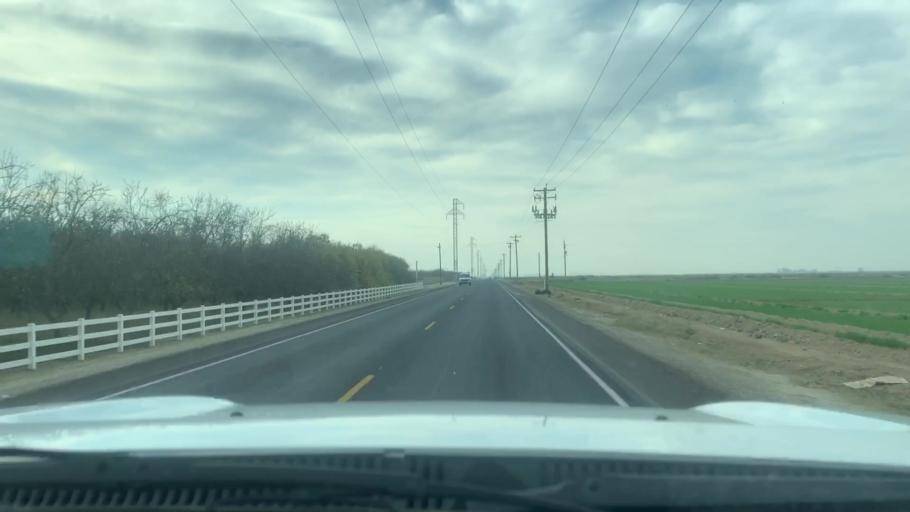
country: US
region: California
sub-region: Kern County
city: Shafter
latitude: 35.4420
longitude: -119.3480
